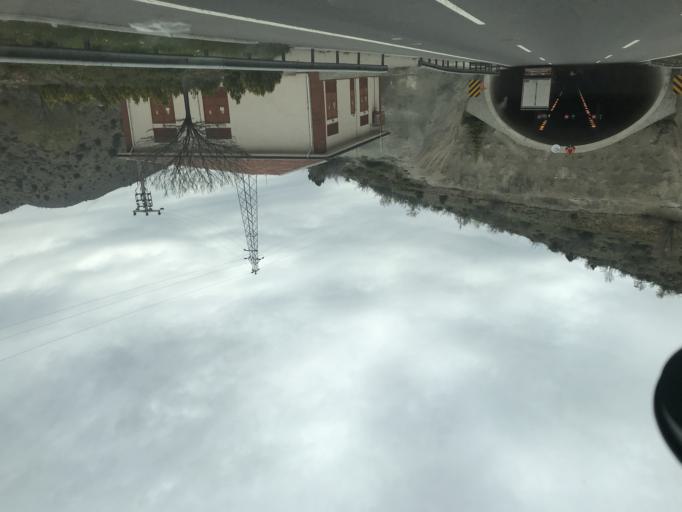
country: TR
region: Nigde
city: Ciftehan
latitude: 37.5741
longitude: 34.7530
